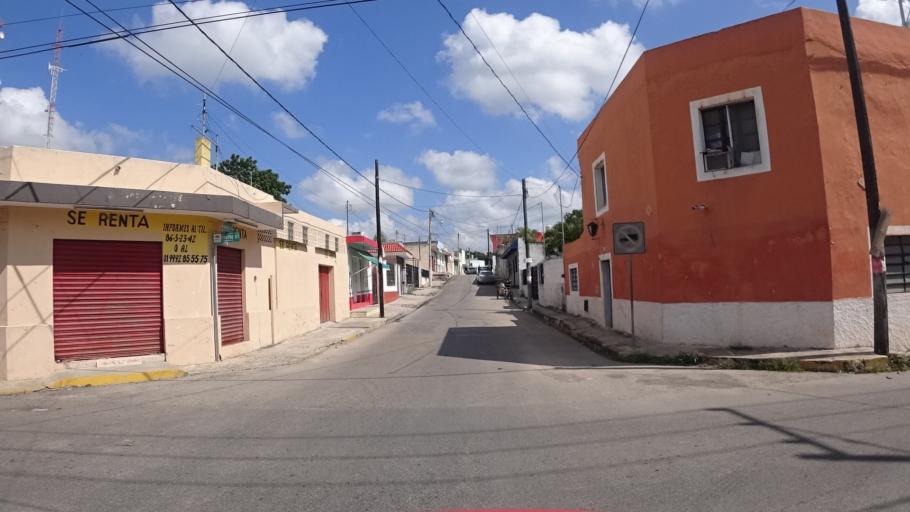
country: MX
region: Yucatan
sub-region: Tizimin
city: Tizimin
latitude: 21.1407
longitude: -88.1528
